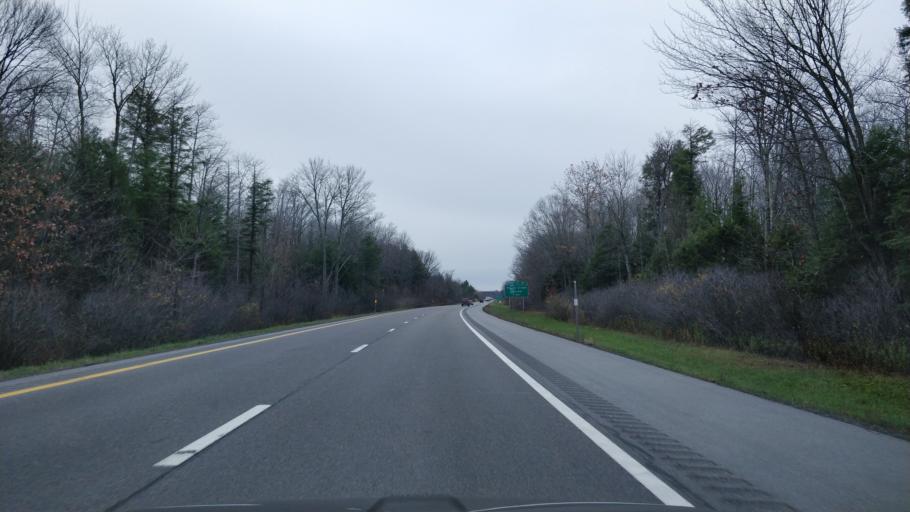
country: US
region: New York
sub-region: Oswego County
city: Pulaski
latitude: 43.6674
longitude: -76.0714
